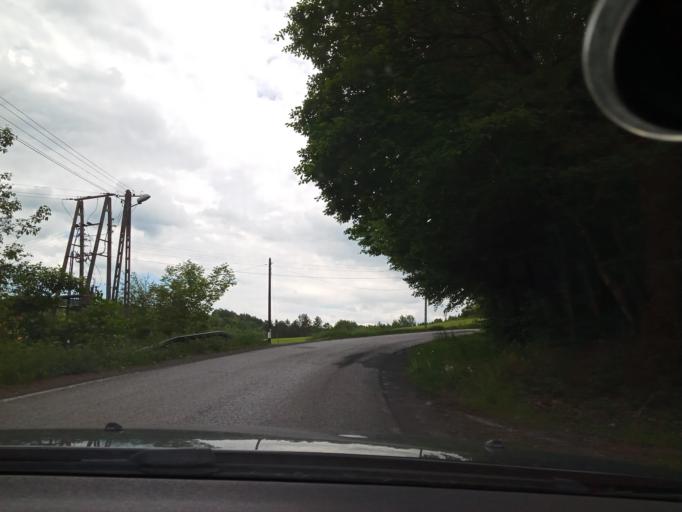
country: PL
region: Lesser Poland Voivodeship
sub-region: Powiat bochenski
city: Lapanow
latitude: 49.8228
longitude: 20.3103
